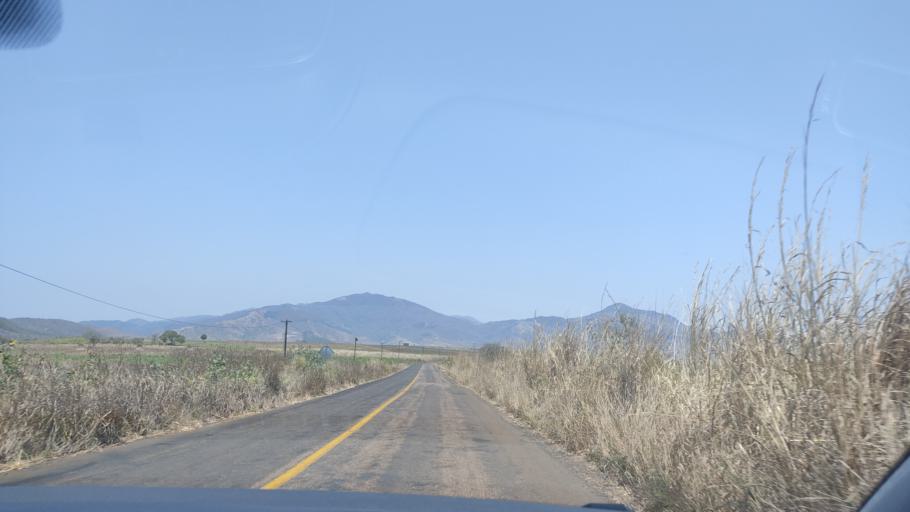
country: MX
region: Nayarit
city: Puga
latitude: 21.5777
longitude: -104.7548
